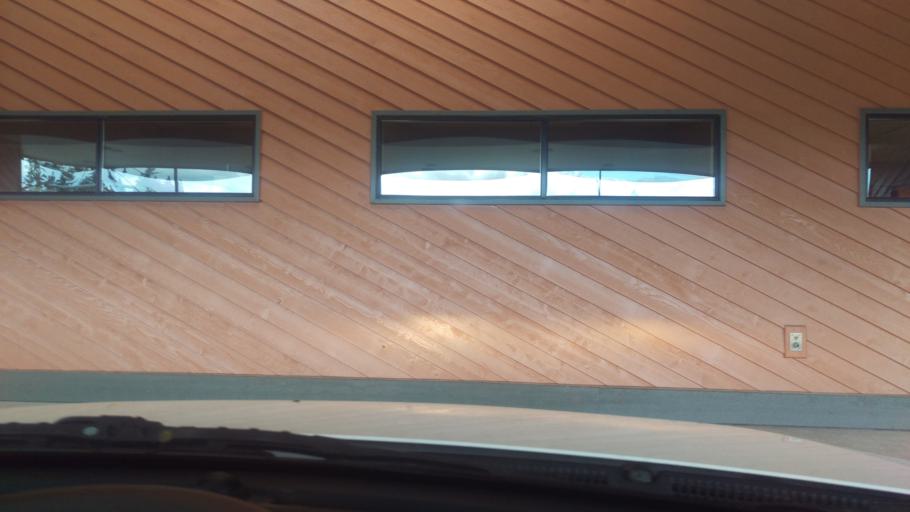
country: US
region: Washington
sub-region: Kitsap County
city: Silverdale
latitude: 47.6503
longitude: -122.6829
